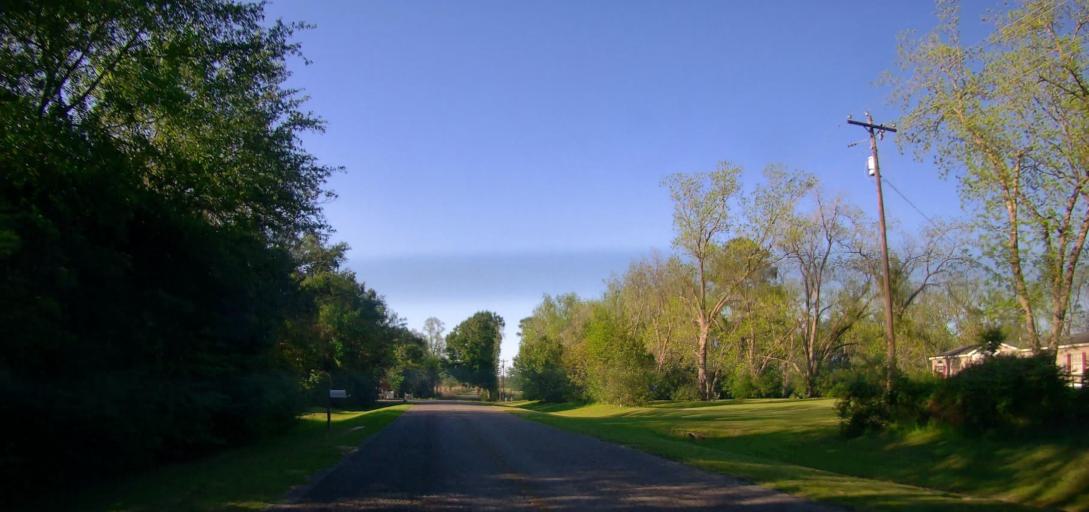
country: US
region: Georgia
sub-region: Ben Hill County
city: Fitzgerald
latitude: 31.6934
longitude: -83.1536
